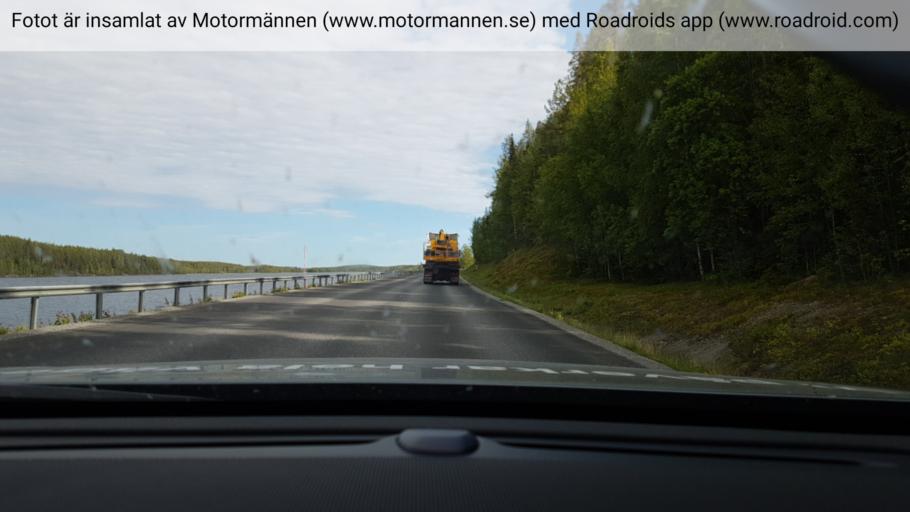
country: SE
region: Vaesterbotten
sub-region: Lycksele Kommun
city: Soderfors
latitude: 64.8486
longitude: 17.9602
